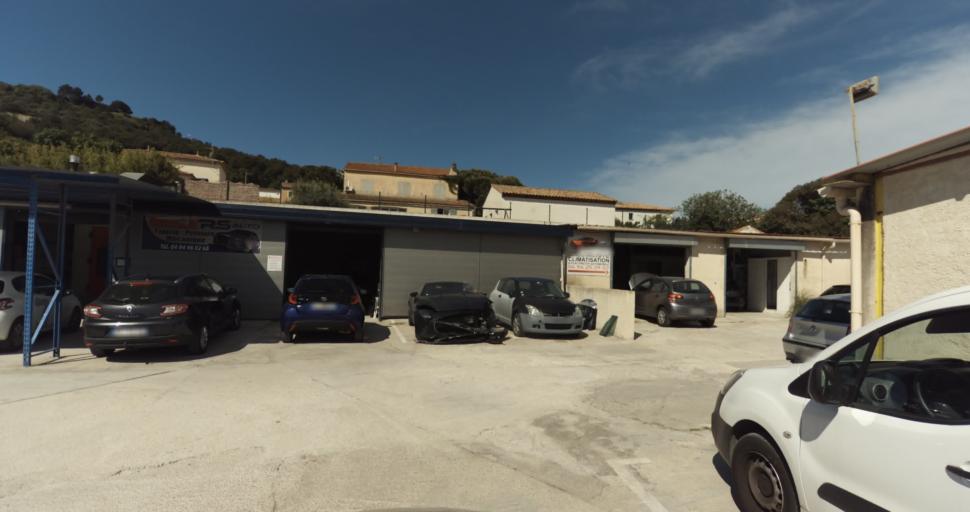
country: FR
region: Provence-Alpes-Cote d'Azur
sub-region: Departement du Var
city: Six-Fours-les-Plages
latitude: 43.1073
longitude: 5.8440
